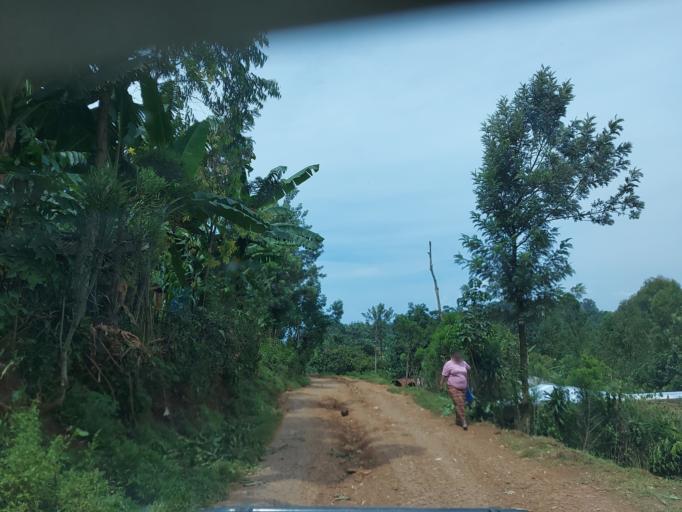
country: CD
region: South Kivu
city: Bukavu
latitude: -2.2356
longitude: 28.8485
